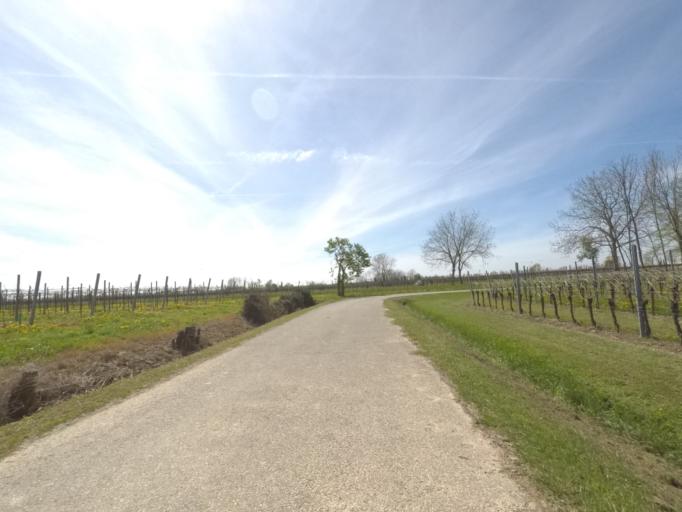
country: IT
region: Friuli Venezia Giulia
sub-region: Provincia di Pordenone
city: Casarsa della Delizia
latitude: 45.9518
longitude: 12.8635
